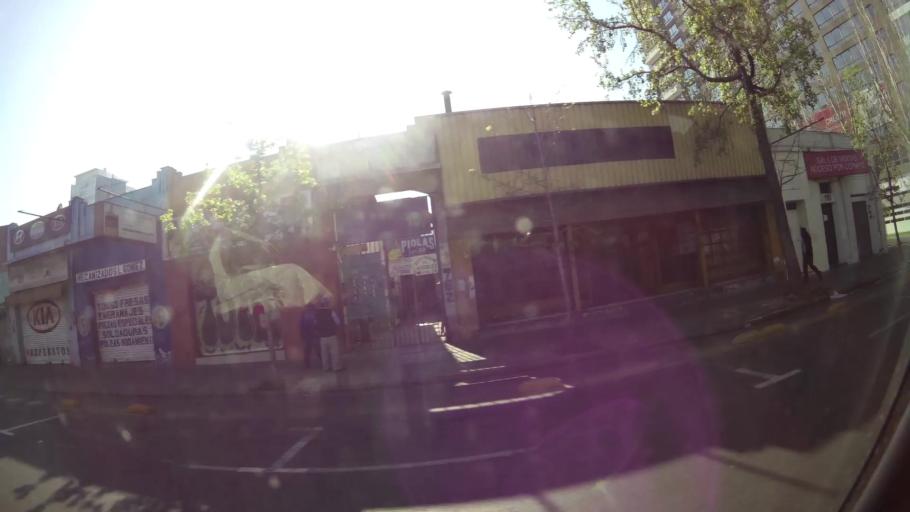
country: CL
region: Santiago Metropolitan
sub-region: Provincia de Santiago
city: Santiago
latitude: -33.4525
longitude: -70.6342
